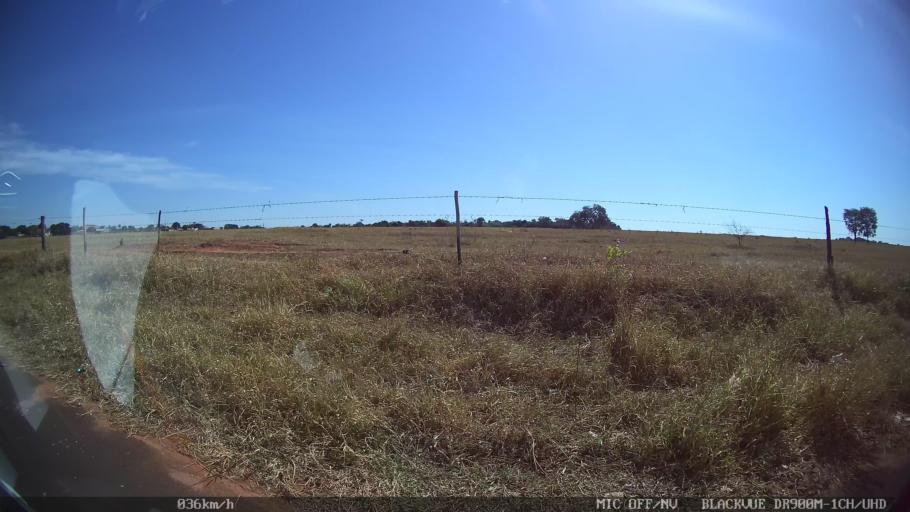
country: BR
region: Sao Paulo
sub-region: Sao Jose Do Rio Preto
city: Sao Jose do Rio Preto
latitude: -20.7483
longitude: -49.4253
